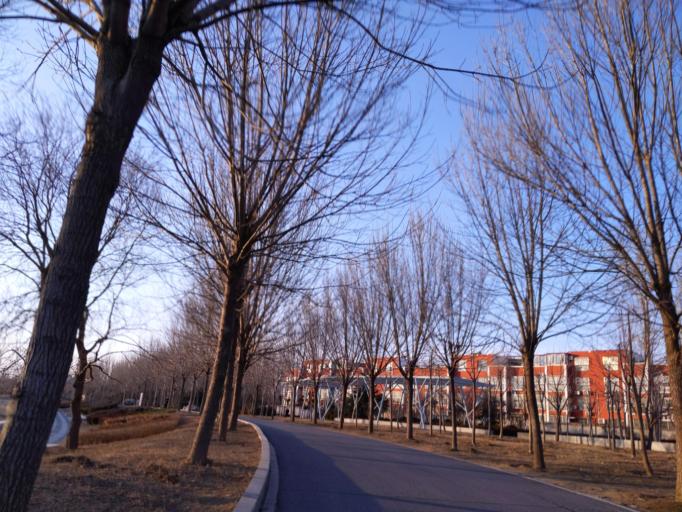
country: CN
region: Henan Sheng
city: Puyang
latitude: 35.7697
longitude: 114.9980
